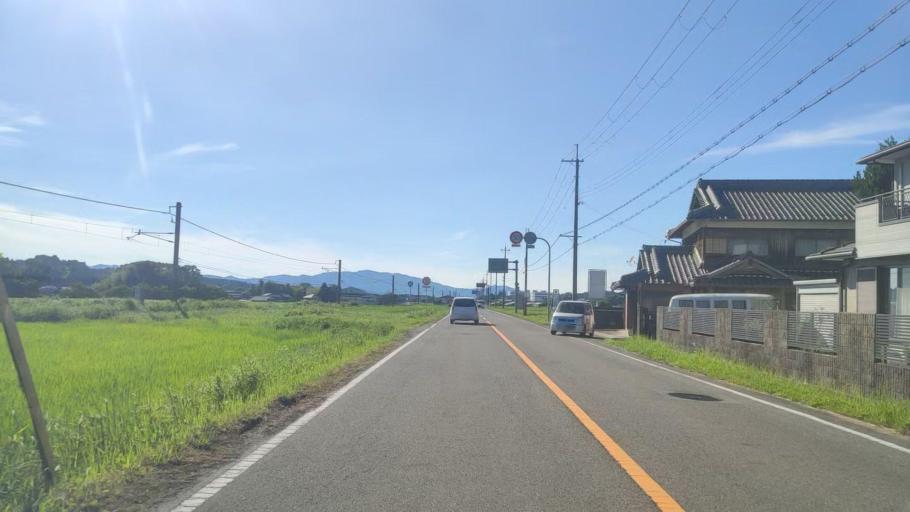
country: JP
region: Shiga Prefecture
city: Minakuchicho-matoba
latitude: 34.8934
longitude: 136.2252
